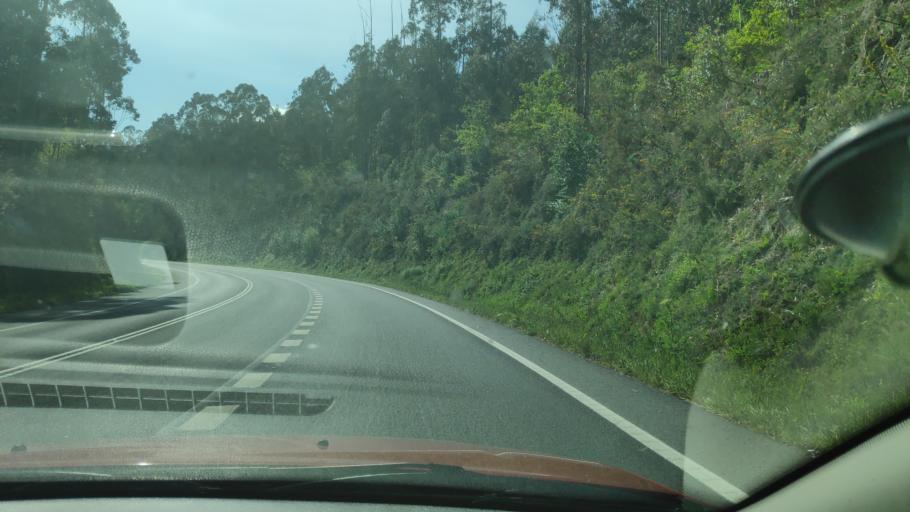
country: ES
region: Galicia
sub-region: Provincia da Coruna
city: Ames
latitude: 42.8799
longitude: -8.6659
